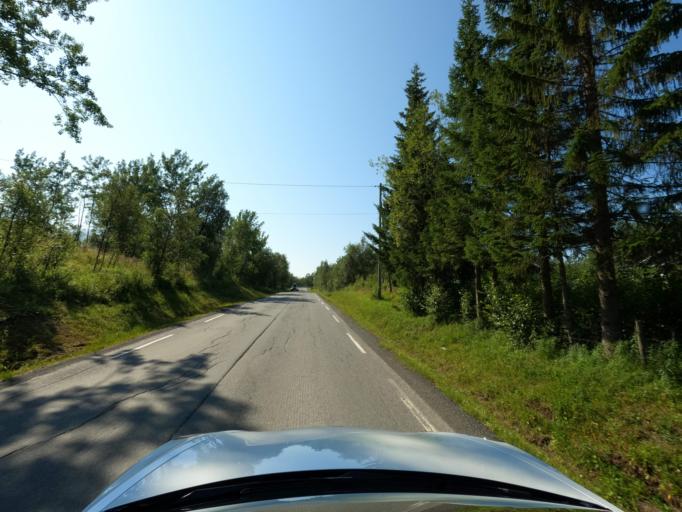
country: NO
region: Nordland
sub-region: Ballangen
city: Ballangen
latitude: 68.3593
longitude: 16.8760
